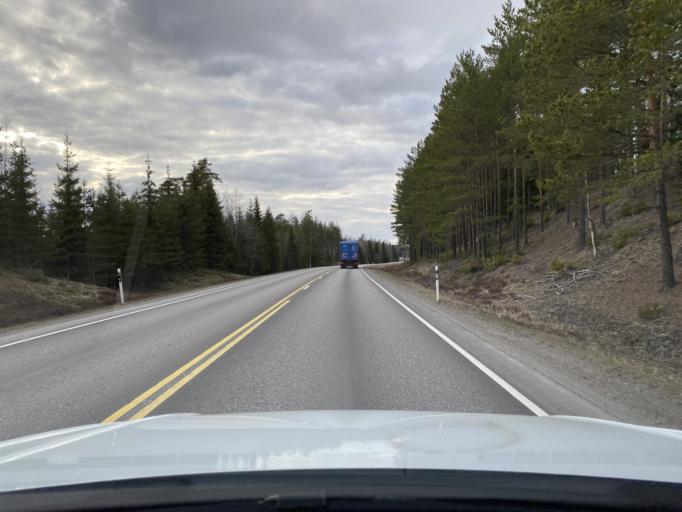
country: FI
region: Uusimaa
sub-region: Helsinki
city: Kaerkoelae
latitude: 60.8222
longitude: 24.0297
